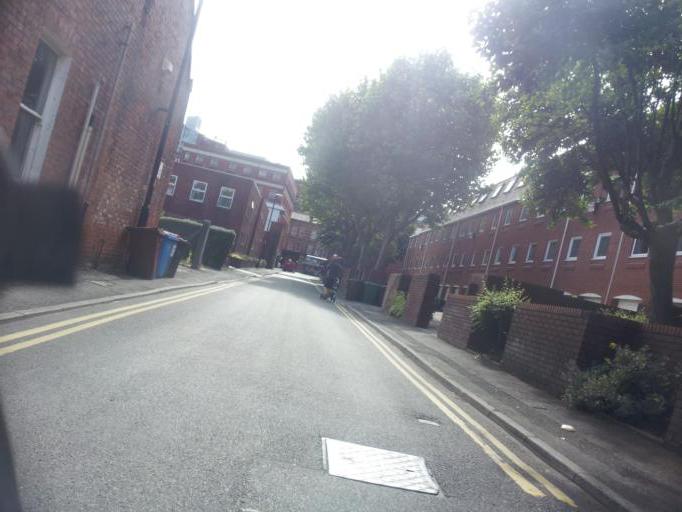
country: GB
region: England
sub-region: Manchester
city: Hulme
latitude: 53.4776
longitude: -2.2523
